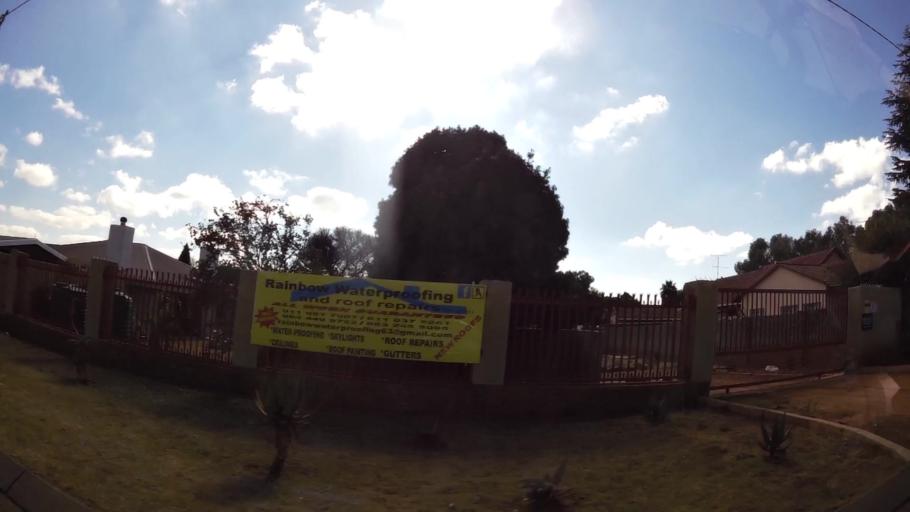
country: ZA
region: Gauteng
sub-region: City of Johannesburg Metropolitan Municipality
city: Roodepoort
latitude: -26.1285
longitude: 27.8386
